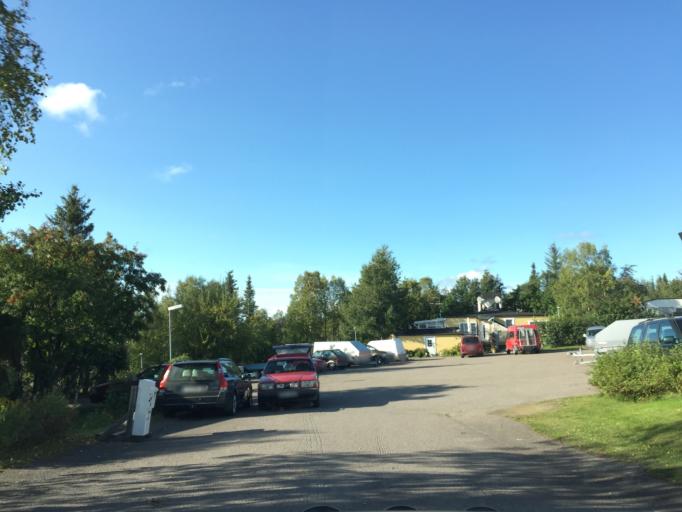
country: SE
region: Norrbotten
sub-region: Gallivare Kommun
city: Malmberget
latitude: 67.6483
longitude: 21.0509
